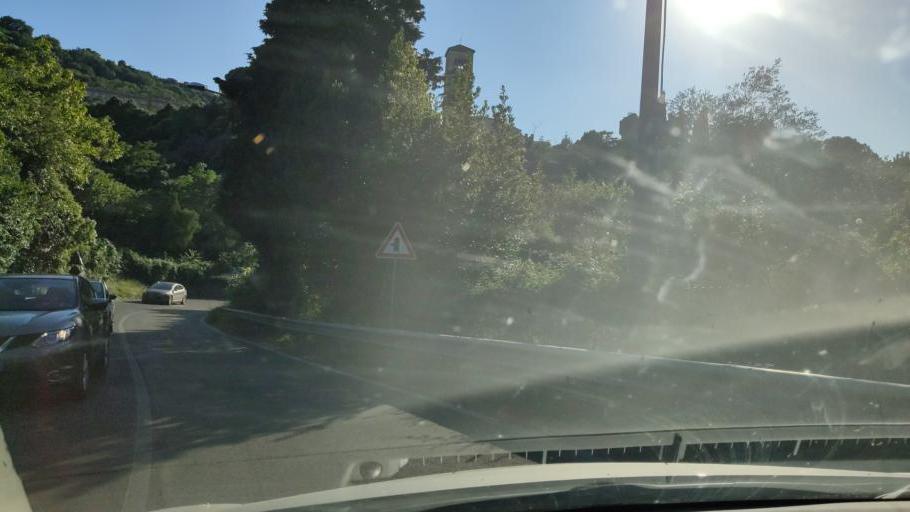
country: IT
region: Umbria
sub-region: Provincia di Terni
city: Narni
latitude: 42.5185
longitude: 12.5261
